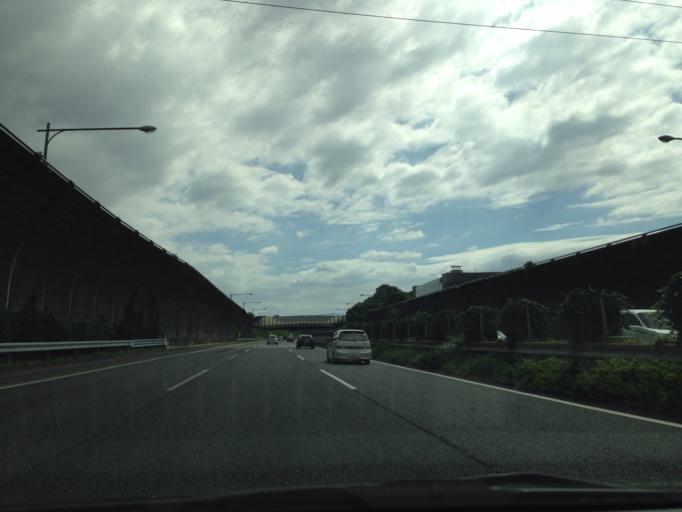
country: JP
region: Kanagawa
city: Isehara
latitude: 35.3901
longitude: 139.2804
